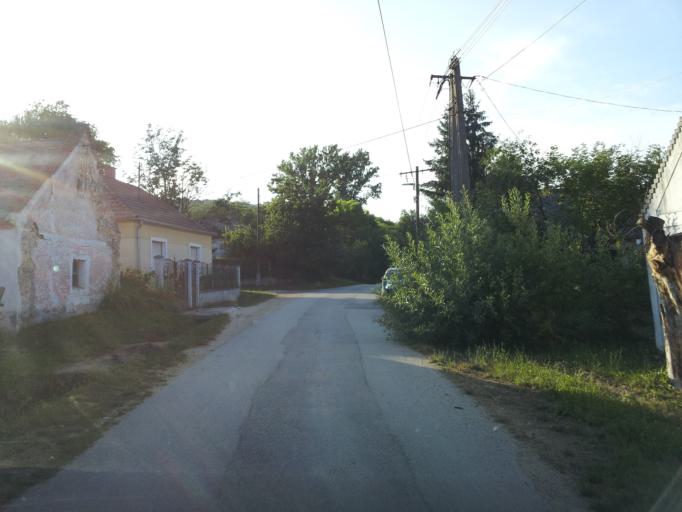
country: HU
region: Veszprem
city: Ajka
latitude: 46.9864
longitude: 17.5663
